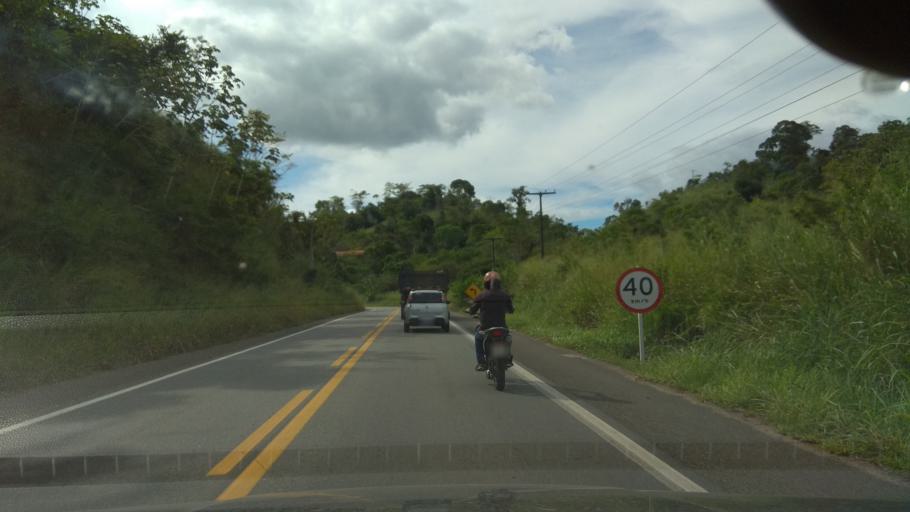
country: BR
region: Bahia
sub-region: Ipiau
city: Ipiau
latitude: -14.0992
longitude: -39.7774
